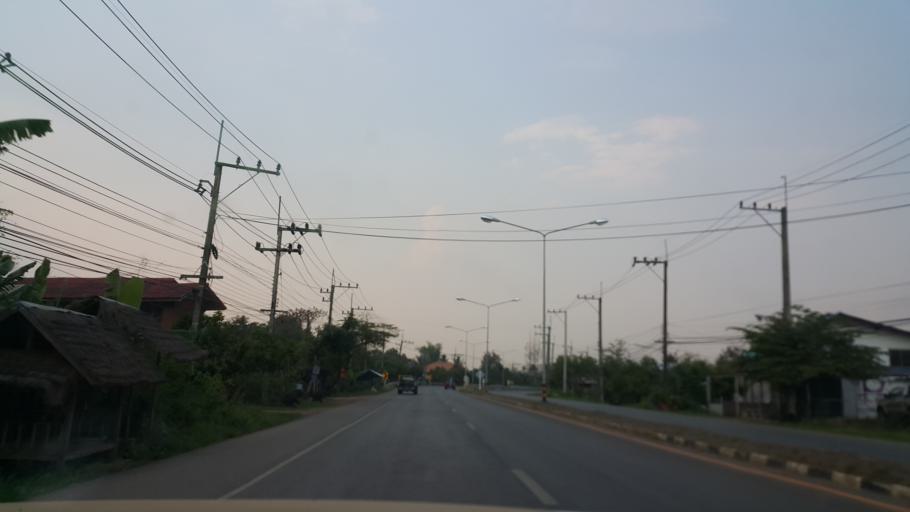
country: TH
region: Nakhon Phanom
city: That Phanom
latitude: 16.9906
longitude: 104.7246
